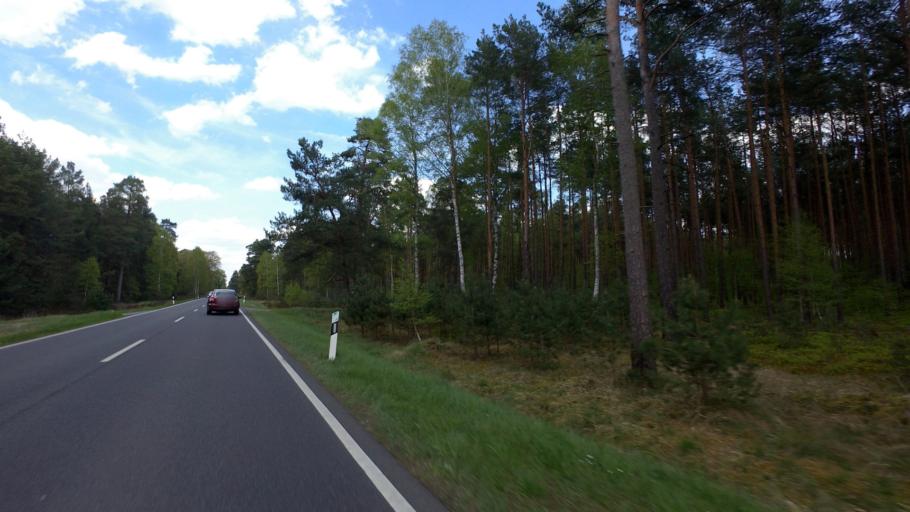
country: DE
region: Brandenburg
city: Marienwerder
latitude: 52.9608
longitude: 13.5695
